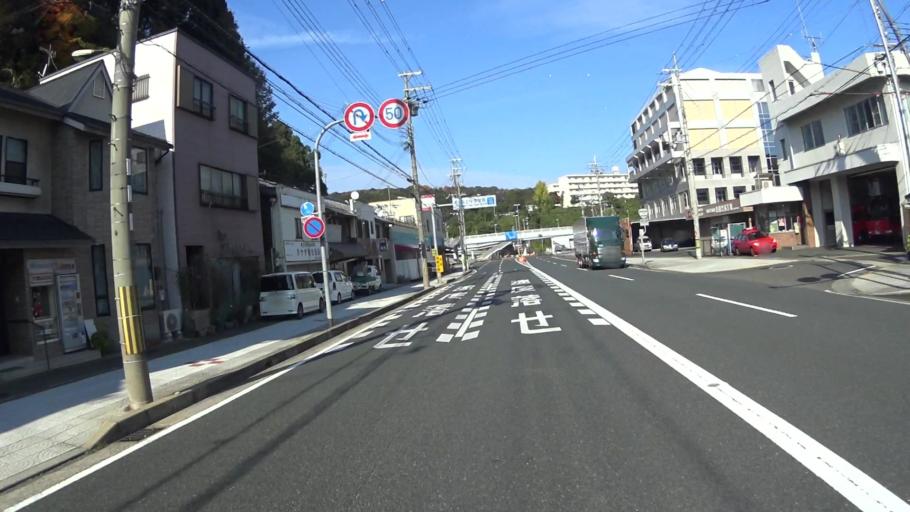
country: JP
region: Kyoto
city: Maizuru
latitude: 35.4748
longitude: 135.3672
